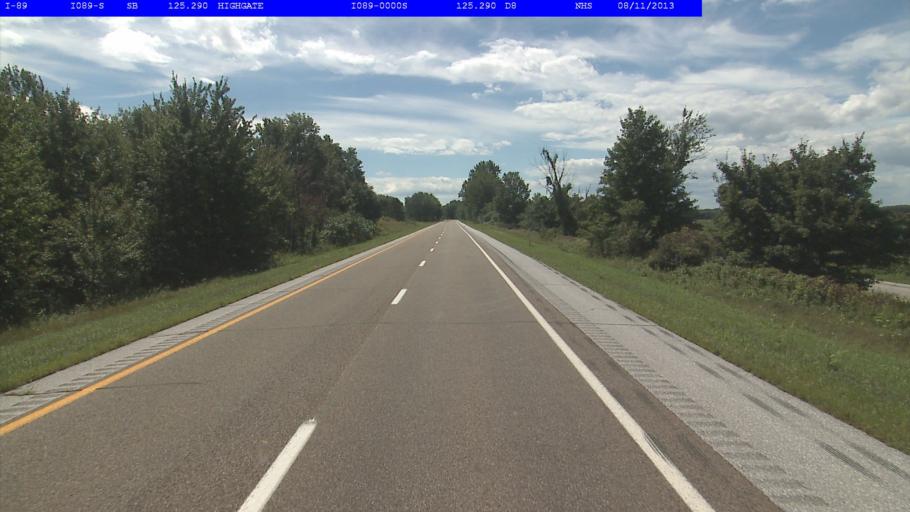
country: US
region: Vermont
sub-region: Franklin County
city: Swanton
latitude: 44.9491
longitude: -73.1131
